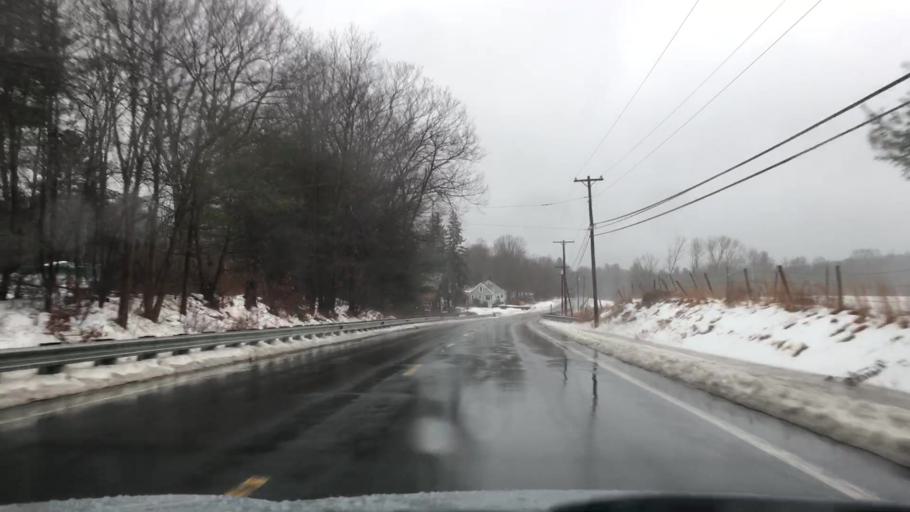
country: US
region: Massachusetts
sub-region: Hampshire County
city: Belchertown
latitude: 42.3093
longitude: -72.4064
